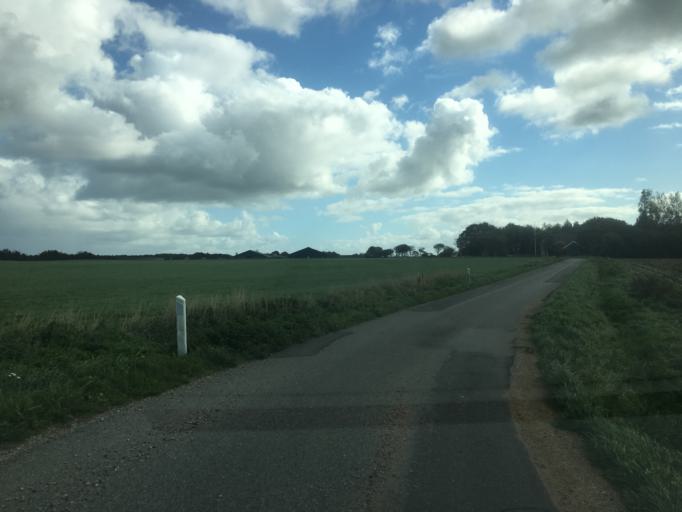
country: DK
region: South Denmark
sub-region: Tonder Kommune
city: Sherrebek
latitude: 55.1167
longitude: 8.8651
